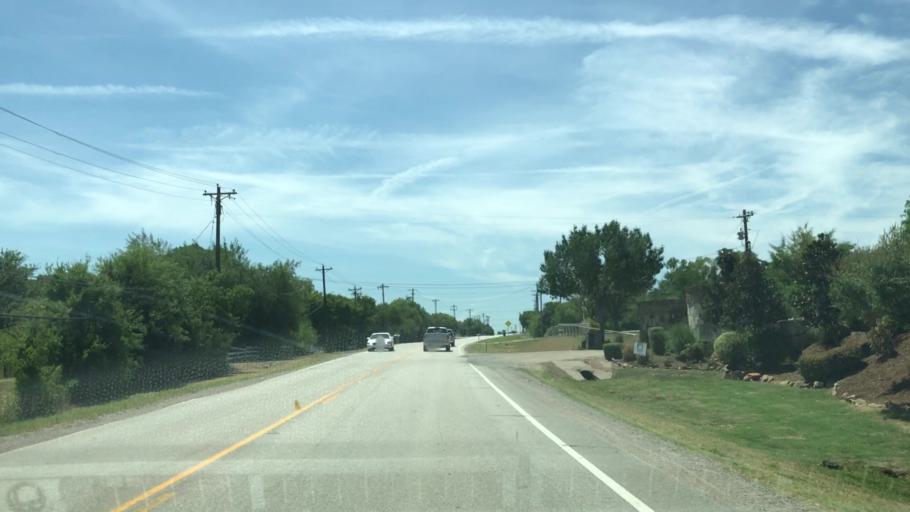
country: US
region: Texas
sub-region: Collin County
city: Saint Paul
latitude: 33.0469
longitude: -96.5496
